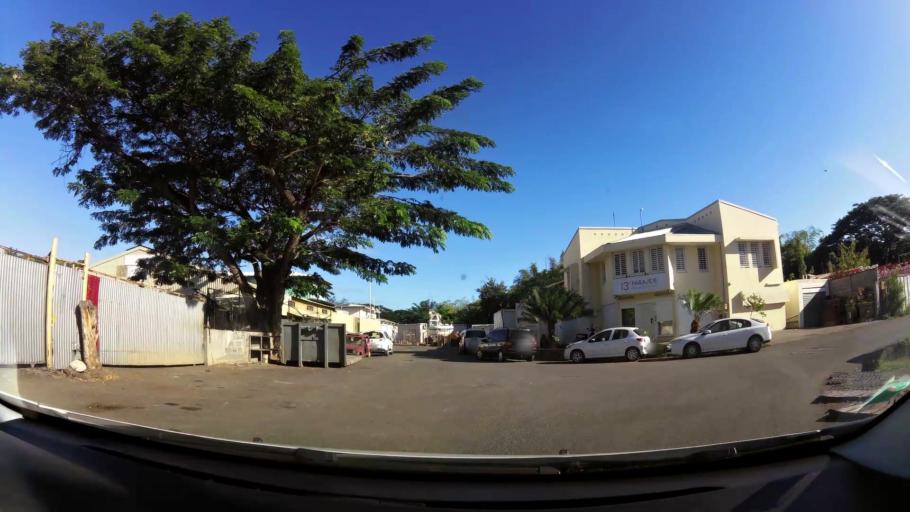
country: YT
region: Mamoudzou
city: Mamoudzou
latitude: -12.7678
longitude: 45.2288
